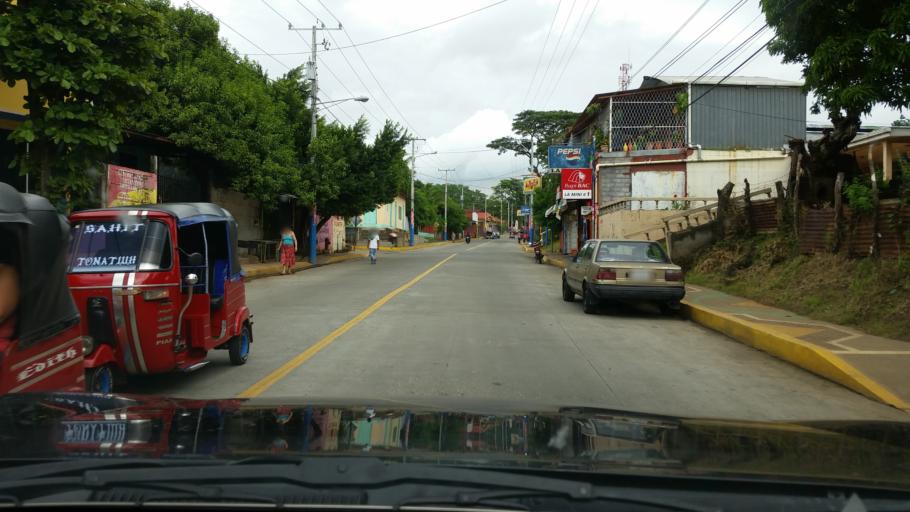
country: NI
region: Masaya
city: Ticuantepe
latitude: 12.0239
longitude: -86.2061
